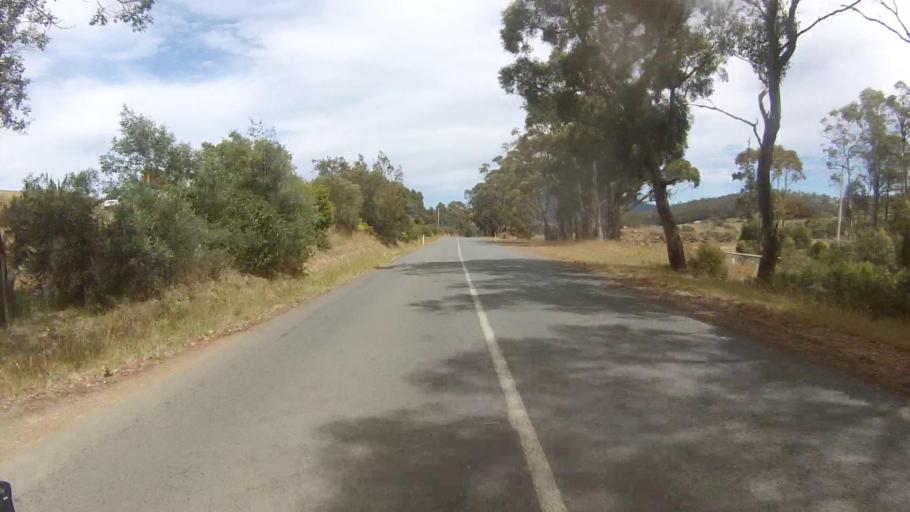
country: AU
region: Tasmania
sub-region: Sorell
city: Sorell
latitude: -42.8194
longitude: 147.8109
